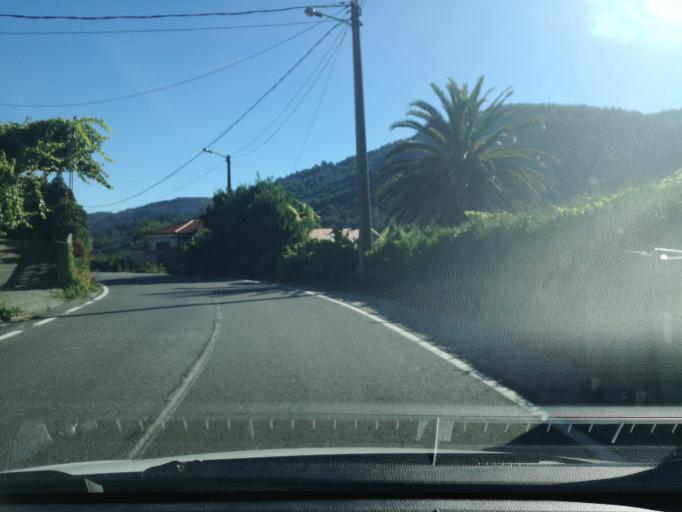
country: ES
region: Galicia
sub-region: Provincia de Ourense
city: Lobios
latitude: 41.8577
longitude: -8.1110
